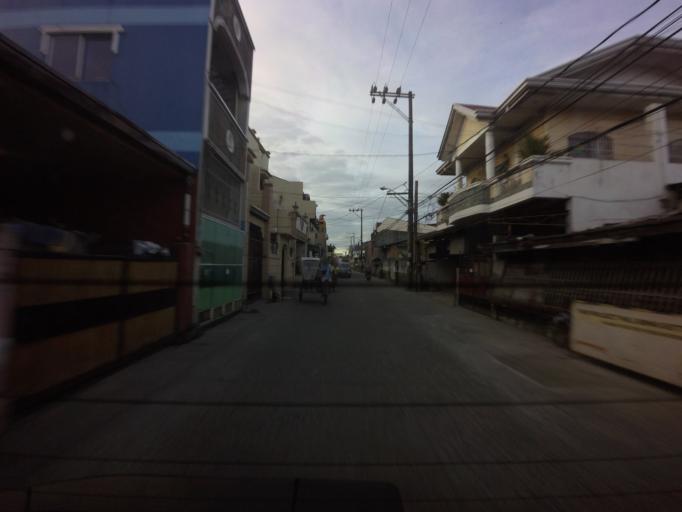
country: PH
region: Central Luzon
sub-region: Province of Bulacan
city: Obando
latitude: 14.7084
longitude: 120.9381
